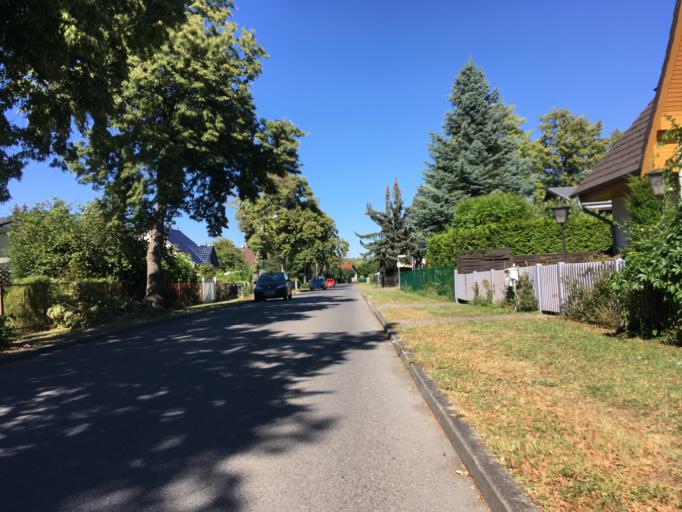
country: DE
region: Brandenburg
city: Schulzendorf
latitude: 52.3612
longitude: 13.5892
